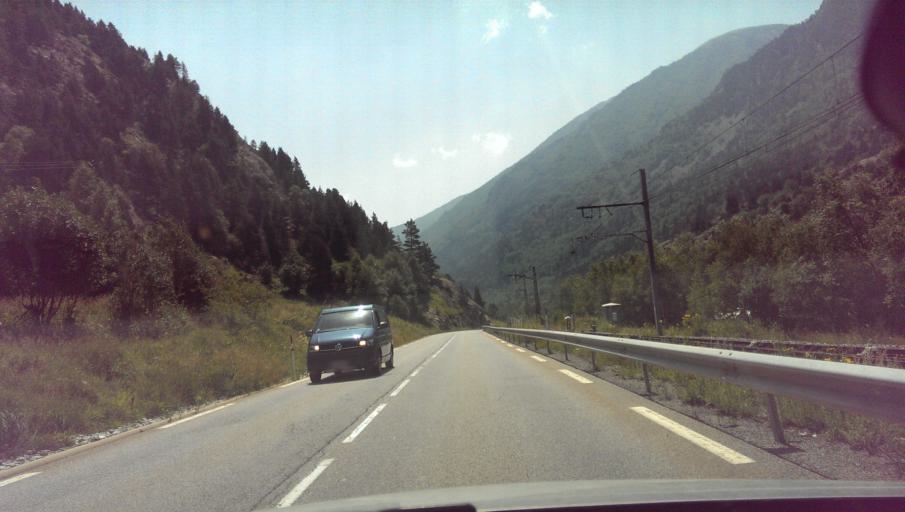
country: ES
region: Catalonia
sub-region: Provincia de Girona
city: Meranges
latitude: 42.5200
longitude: 1.8224
